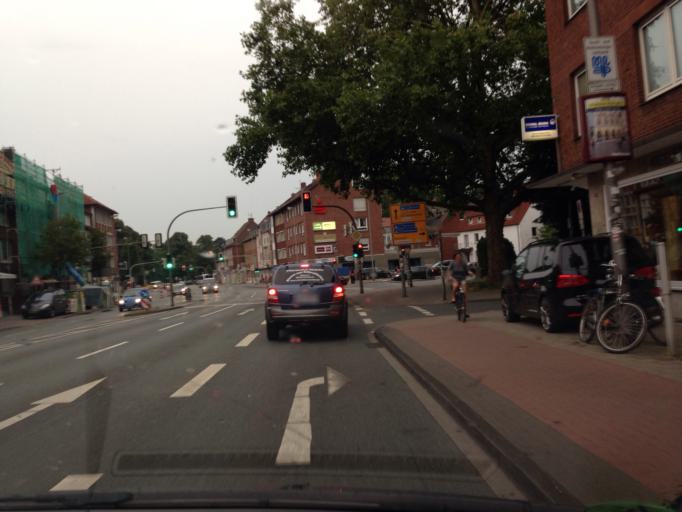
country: DE
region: North Rhine-Westphalia
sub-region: Regierungsbezirk Munster
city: Muenster
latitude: 51.9544
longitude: 7.6200
